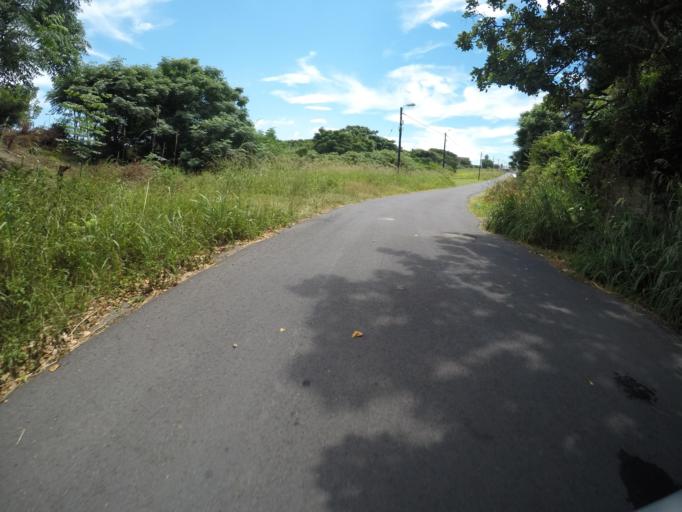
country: ZA
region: Eastern Cape
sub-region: Buffalo City Metropolitan Municipality
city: East London
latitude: -33.0400
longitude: 27.8482
